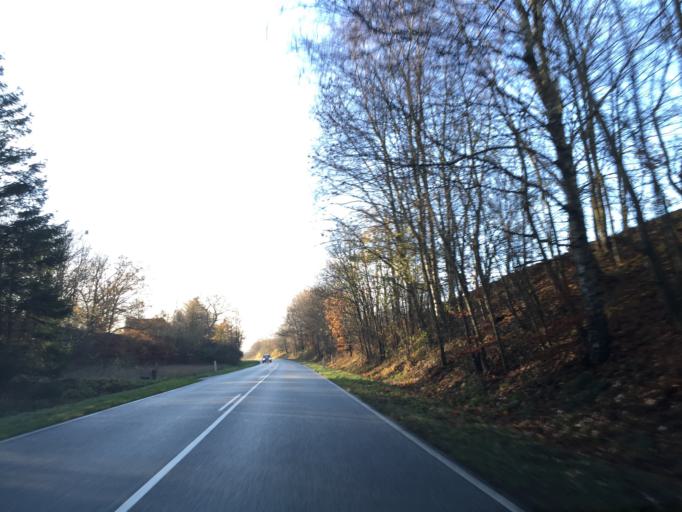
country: DK
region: Central Jutland
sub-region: Skanderborg Kommune
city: Galten
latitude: 56.1768
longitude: 9.8332
